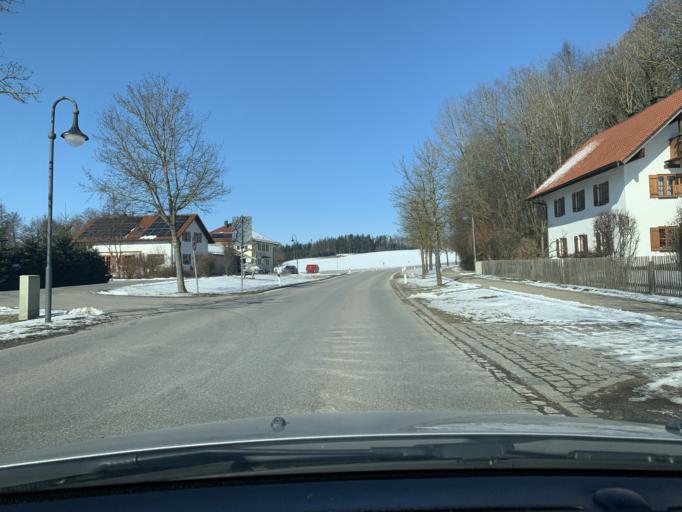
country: DE
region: Bavaria
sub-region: Upper Bavaria
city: Zangberg
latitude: 48.2750
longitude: 12.4241
